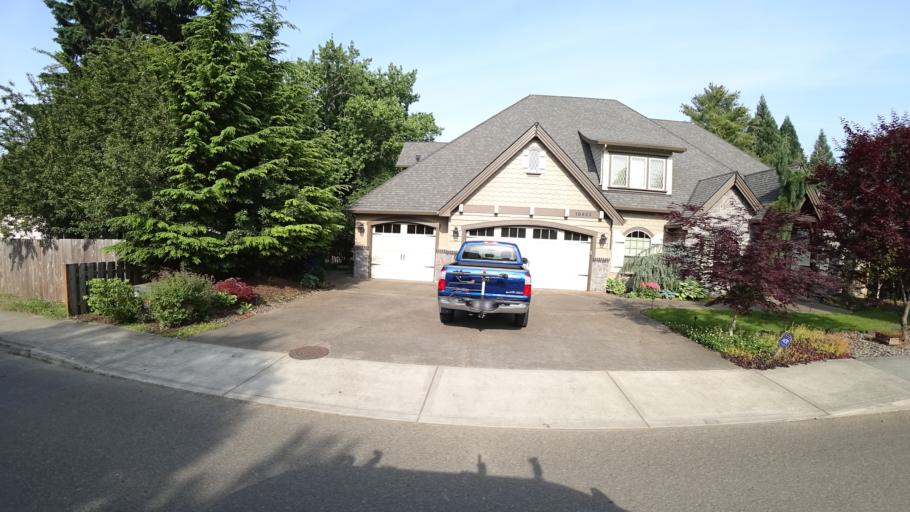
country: US
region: Oregon
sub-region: Clackamas County
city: Happy Valley
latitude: 45.4473
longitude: -122.5220
